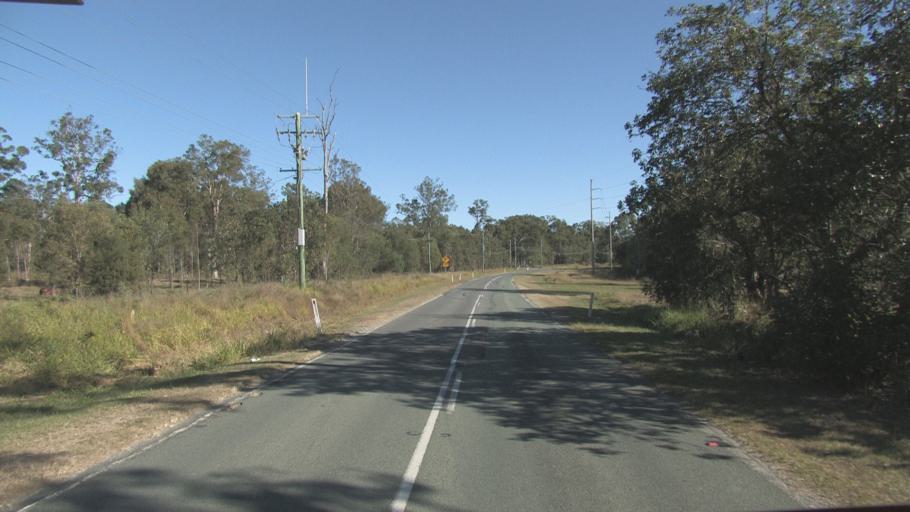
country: AU
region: Queensland
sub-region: Logan
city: North Maclean
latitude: -27.7892
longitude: 153.0433
